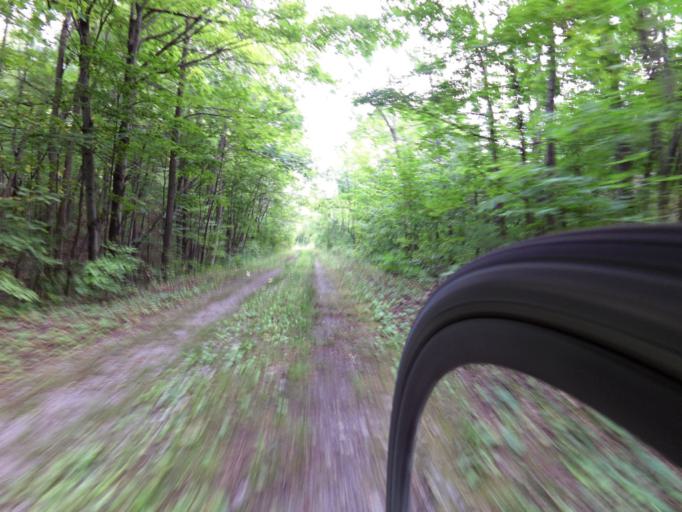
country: CA
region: Ontario
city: Gananoque
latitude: 44.5797
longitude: -76.3243
